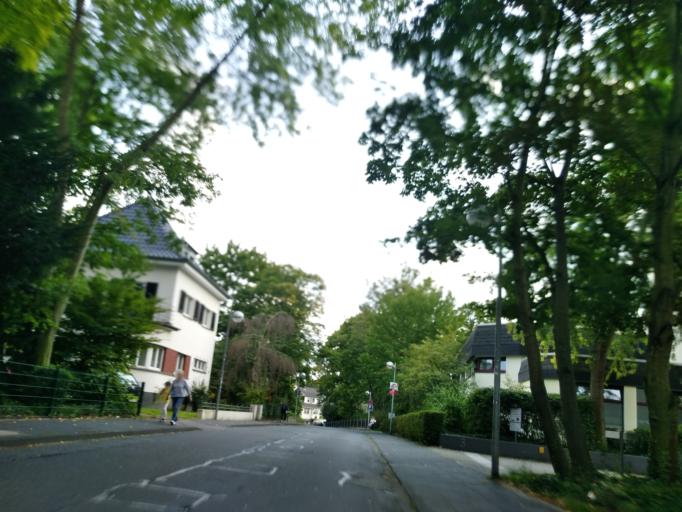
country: DE
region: North Rhine-Westphalia
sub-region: Regierungsbezirk Koln
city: Bad Honnef
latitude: 50.6452
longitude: 7.2230
